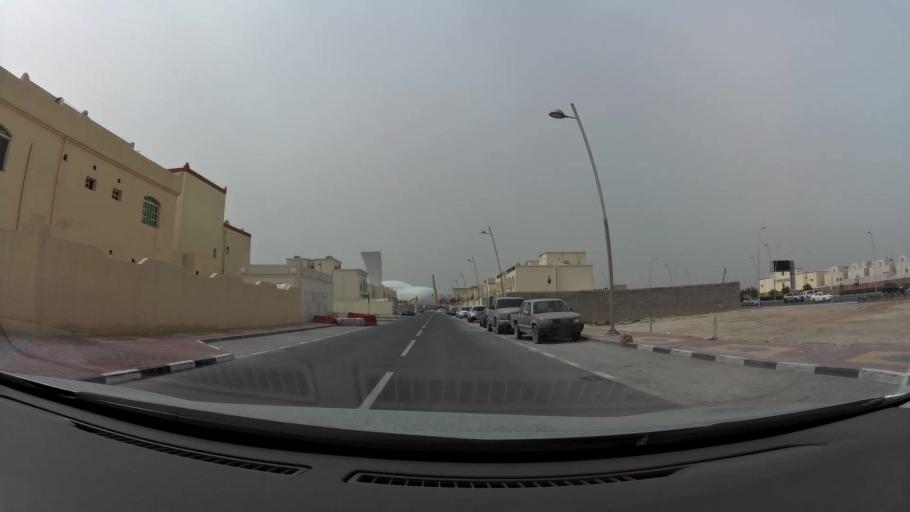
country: QA
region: Baladiyat ad Dawhah
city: Doha
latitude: 25.2348
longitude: 51.5499
